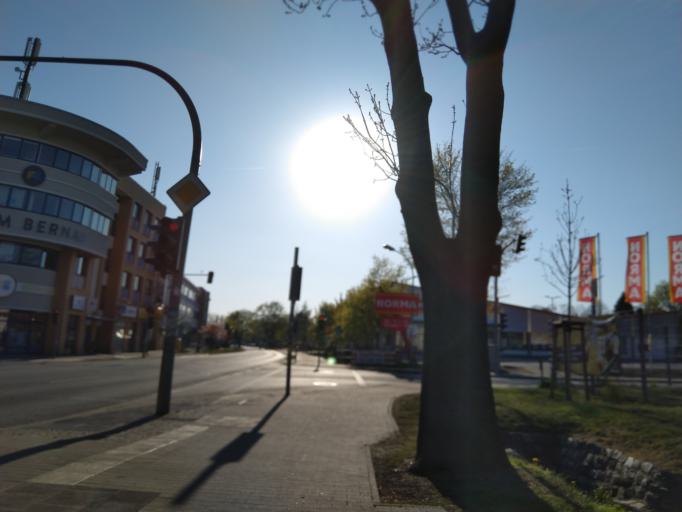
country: DE
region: Brandenburg
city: Bernau bei Berlin
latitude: 52.6749
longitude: 13.5742
